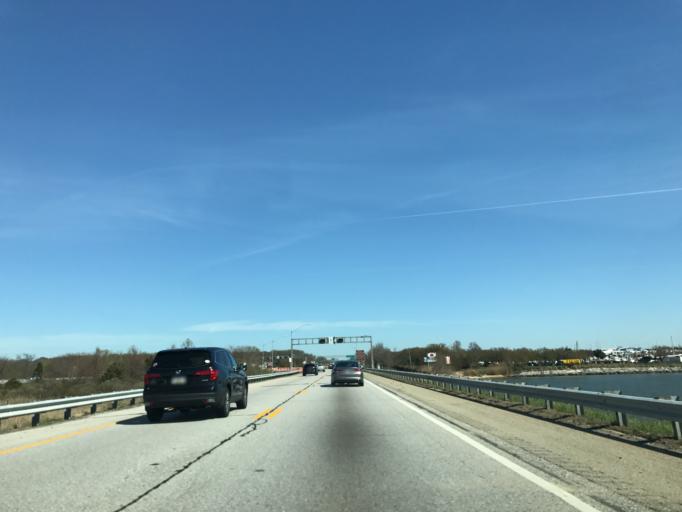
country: US
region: Maryland
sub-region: Queen Anne's County
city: Stevensville
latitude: 38.9826
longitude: -76.3366
